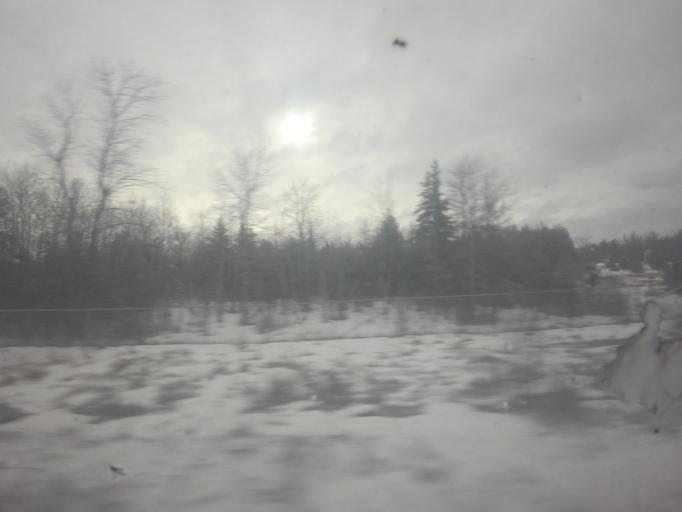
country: CA
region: Ontario
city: Bells Corners
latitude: 45.1204
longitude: -75.8688
